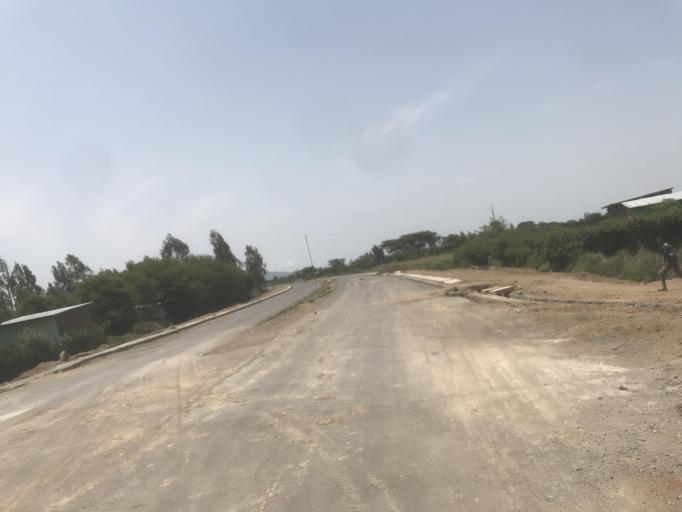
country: ET
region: Oromiya
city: Mojo
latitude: 8.2956
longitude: 38.9399
